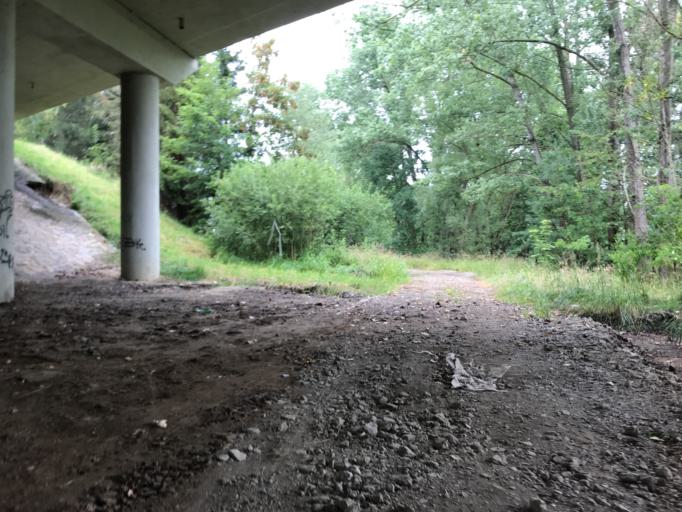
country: CZ
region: Jihocesky
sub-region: Okres Jindrichuv Hradec
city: Trebon
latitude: 49.0104
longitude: 14.7656
